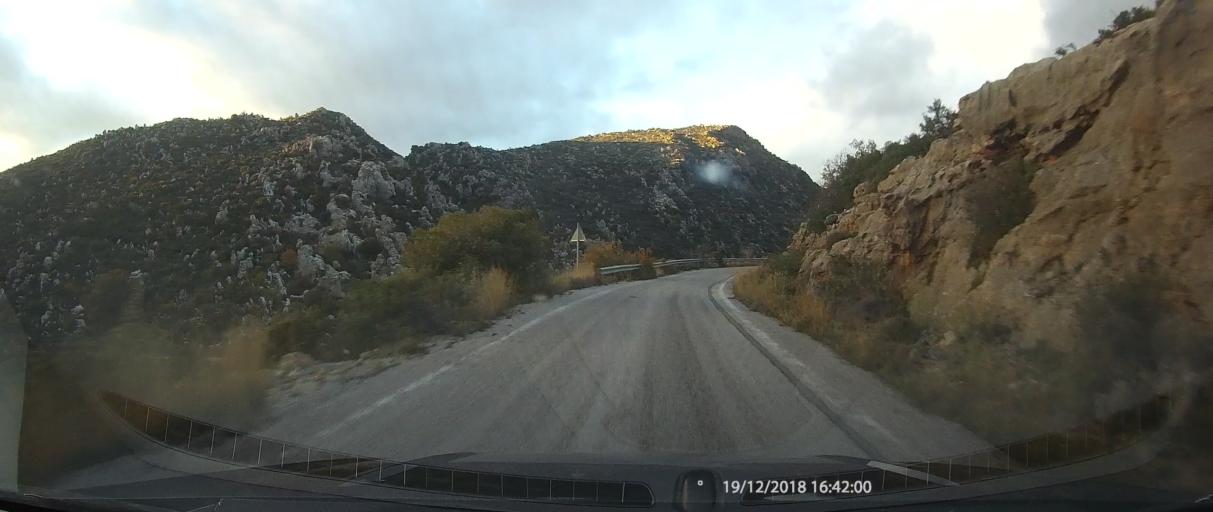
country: GR
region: Peloponnese
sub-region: Nomos Lakonias
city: Sykea
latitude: 36.9019
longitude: 22.9974
